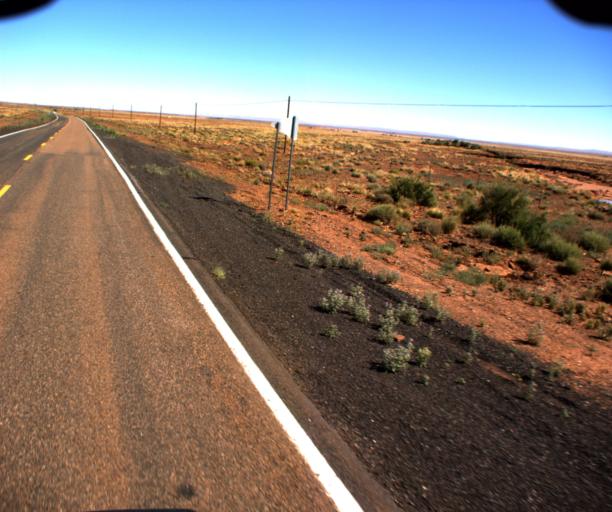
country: US
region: Arizona
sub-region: Coconino County
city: LeChee
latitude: 35.1417
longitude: -110.8917
